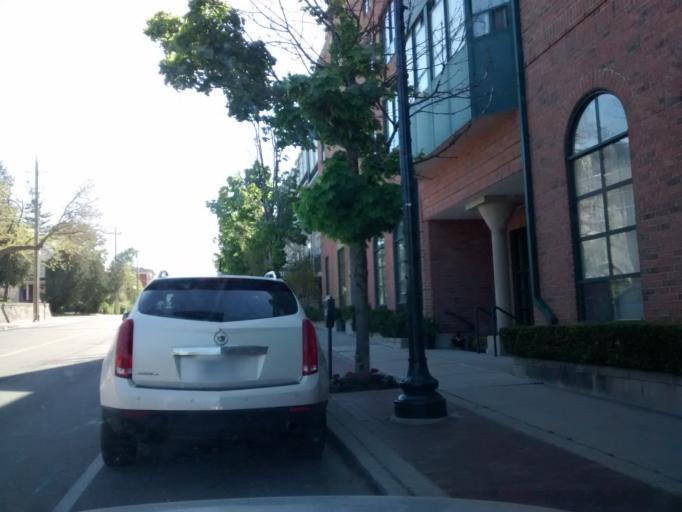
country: CA
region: Ontario
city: Oakville
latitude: 43.4450
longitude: -79.6678
